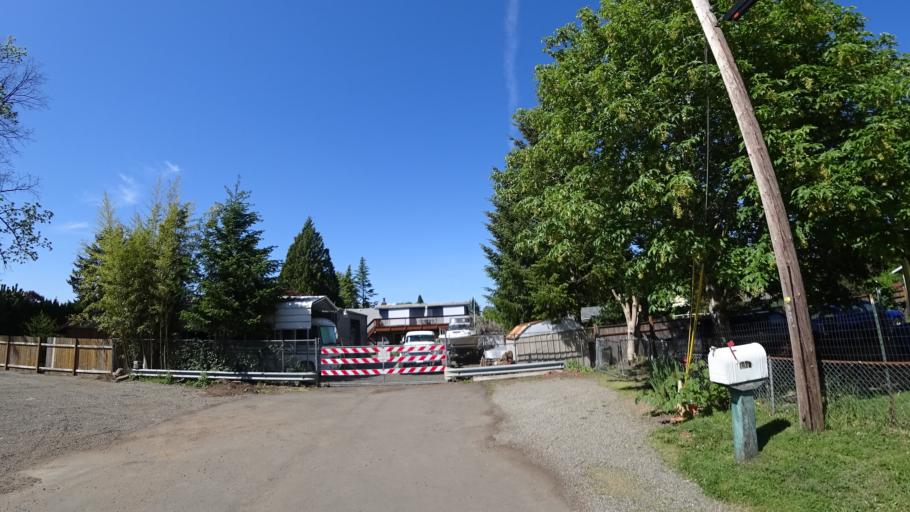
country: US
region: Oregon
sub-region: Washington County
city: Hillsboro
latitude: 45.5100
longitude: -122.9643
